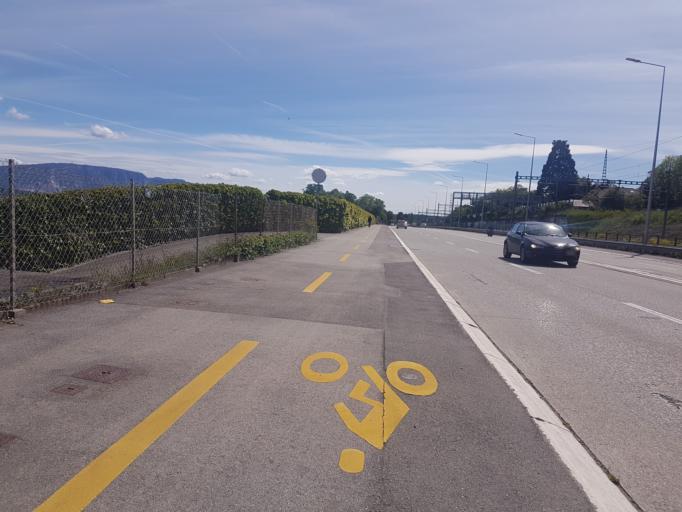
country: CH
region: Geneva
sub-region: Geneva
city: Bellevue
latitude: 46.2671
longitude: 6.1636
